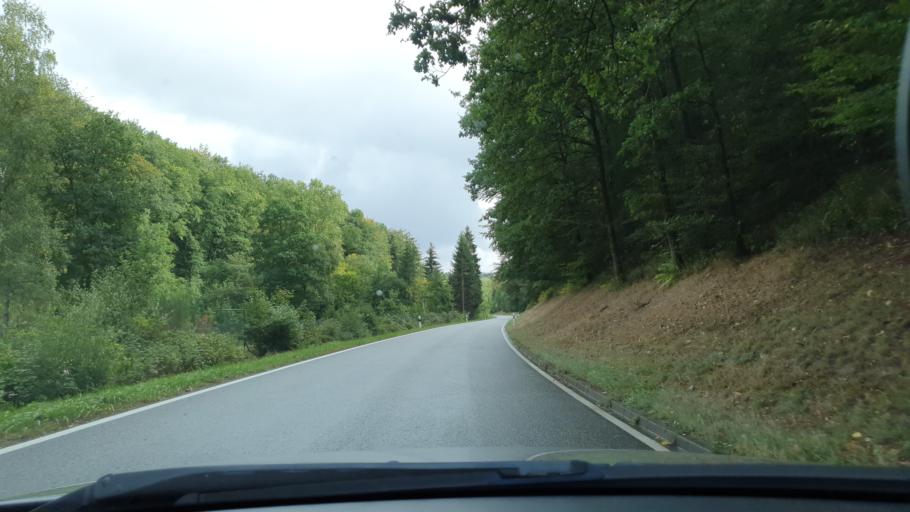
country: DE
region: Rheinland-Pfalz
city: Gerhardsbrunn
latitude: 49.3420
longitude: 7.5171
